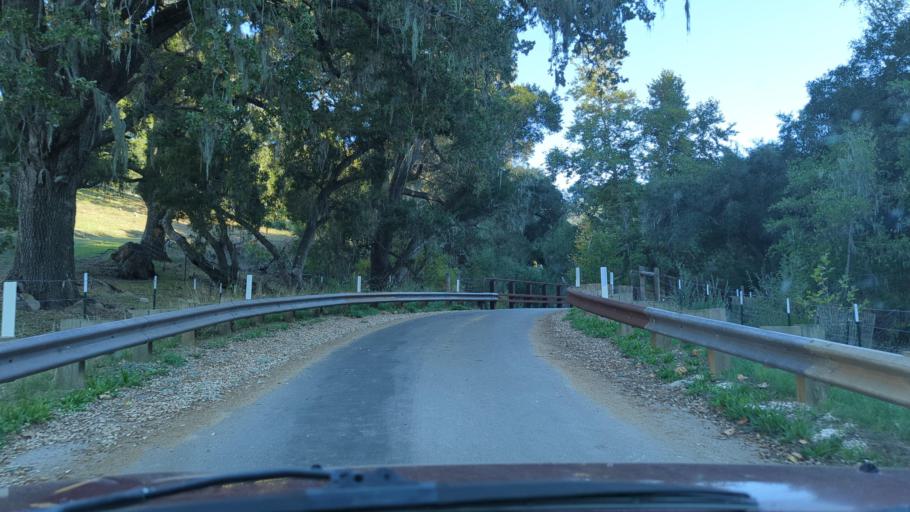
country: US
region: California
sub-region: Santa Barbara County
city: Santa Ynez
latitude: 34.5604
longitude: -120.0854
